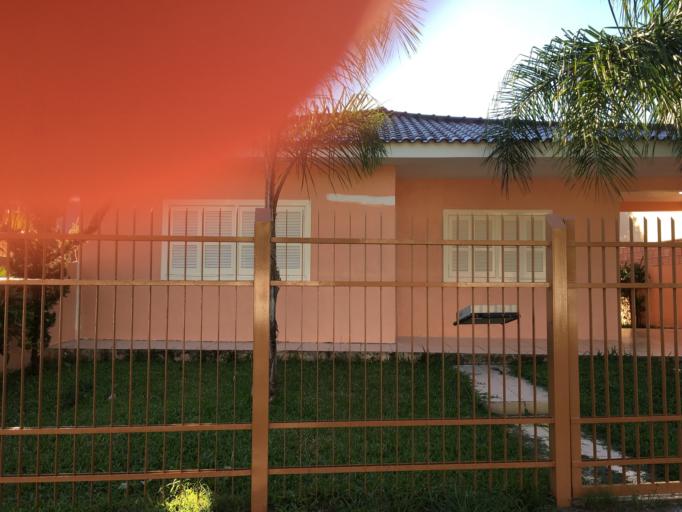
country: BR
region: Rio Grande do Sul
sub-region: Santa Maria
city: Santa Maria
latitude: -29.7008
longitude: -53.7076
